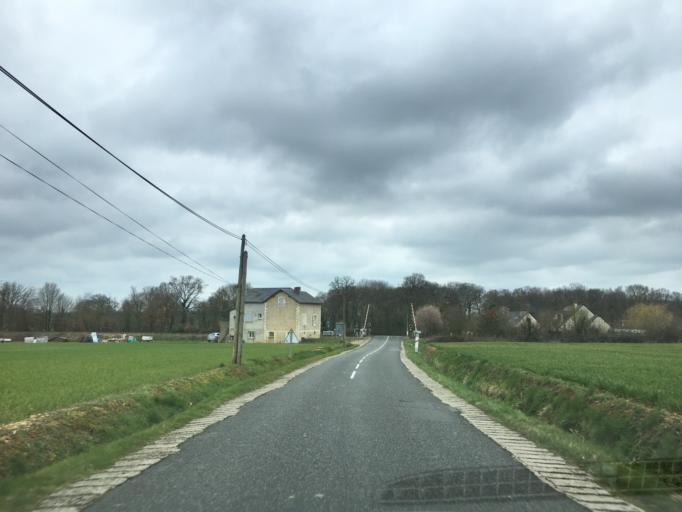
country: FR
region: Centre
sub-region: Departement d'Indre-et-Loire
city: Chanceaux-sur-Choisille
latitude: 47.4703
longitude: 0.7345
